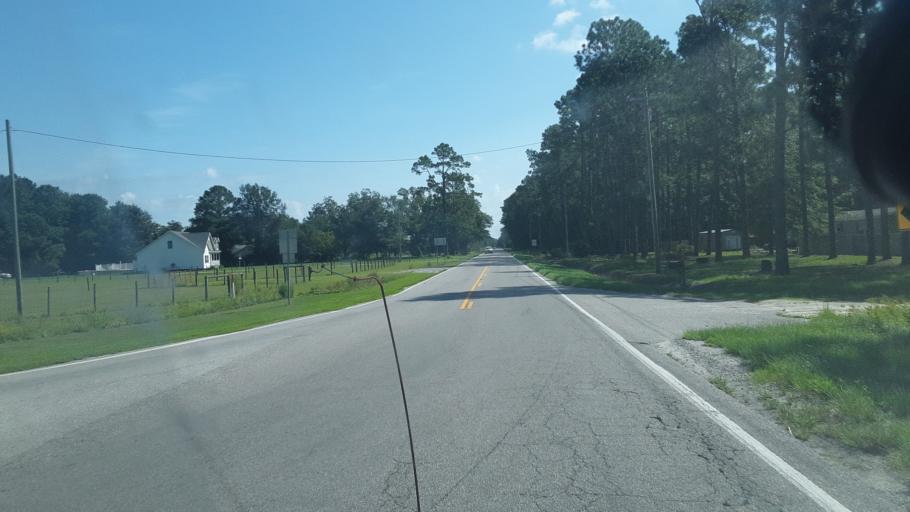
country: US
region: South Carolina
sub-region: Hampton County
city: Varnville
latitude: 32.8772
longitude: -81.0400
